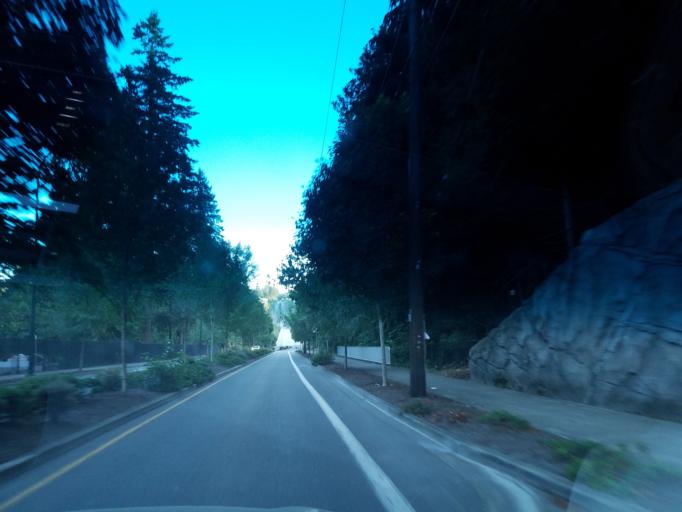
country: US
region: Washington
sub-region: King County
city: City of Sammamish
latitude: 47.6162
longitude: -122.0140
